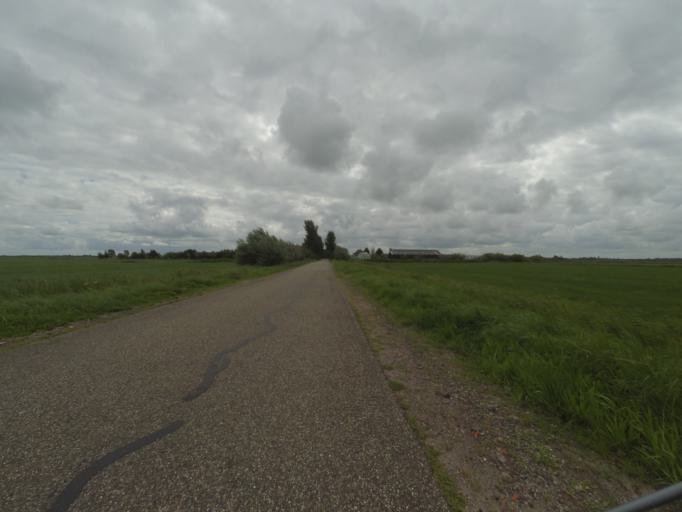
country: NL
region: Friesland
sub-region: Gemeente Kollumerland en Nieuwkruisland
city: Kollumerzwaag
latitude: 53.3100
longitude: 6.0894
